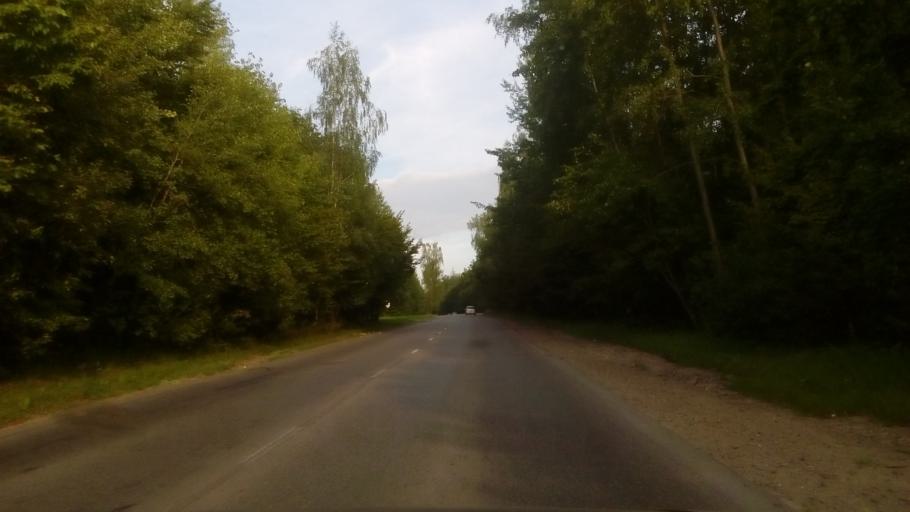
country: LT
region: Alytaus apskritis
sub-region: Alytus
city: Alytus
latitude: 54.3870
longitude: 24.0042
